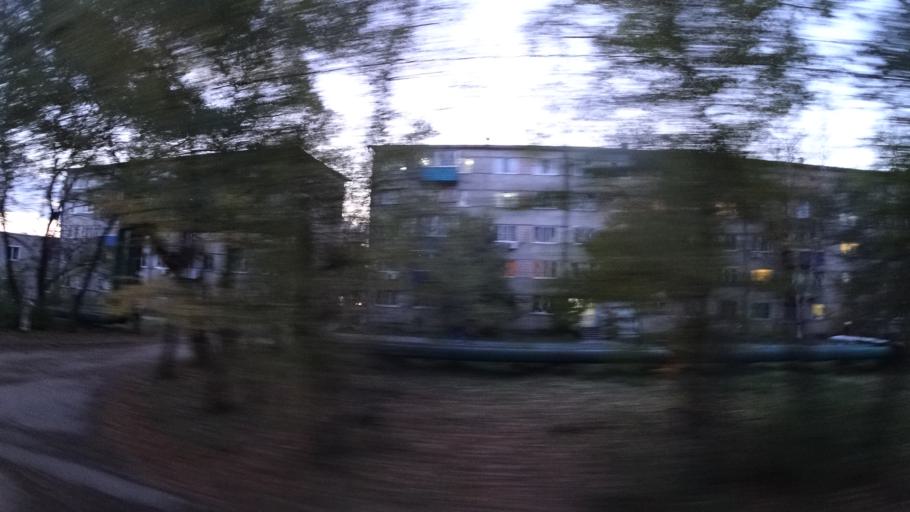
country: RU
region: Khabarovsk Krai
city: Amursk
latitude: 50.2162
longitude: 136.9013
